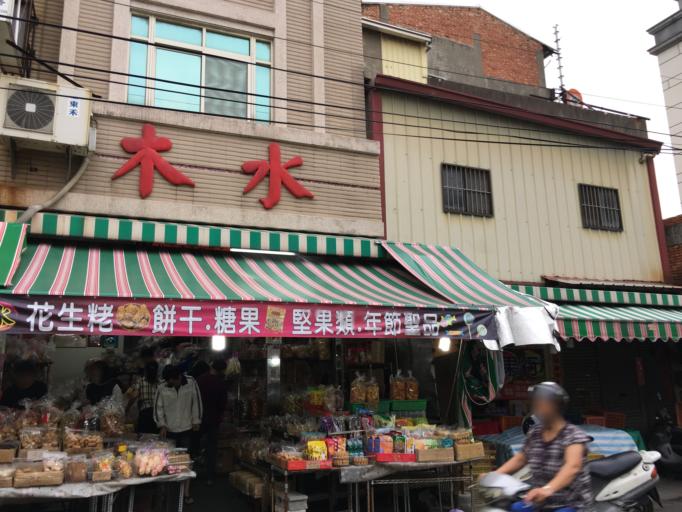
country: TW
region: Taiwan
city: Fengyuan
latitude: 24.3475
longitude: 120.6252
